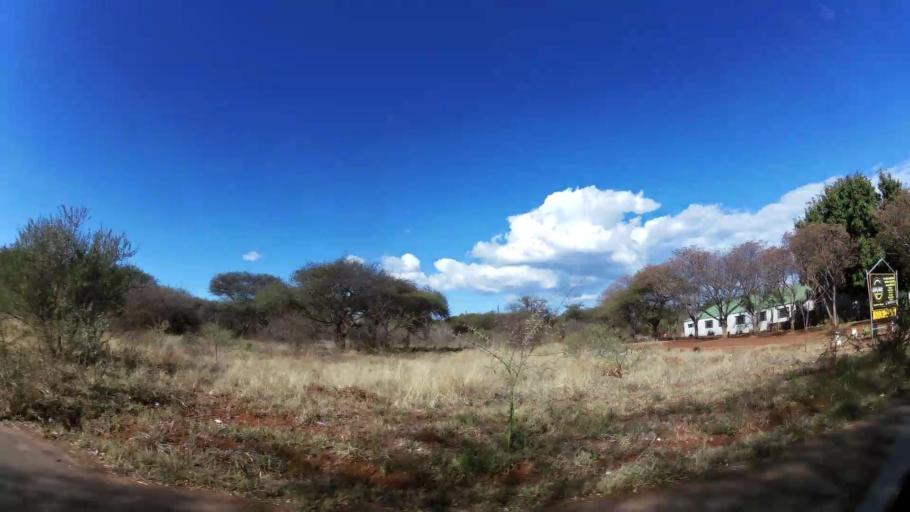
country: ZA
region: Limpopo
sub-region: Waterberg District Municipality
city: Mokopane
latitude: -24.1906
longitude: 29.0171
